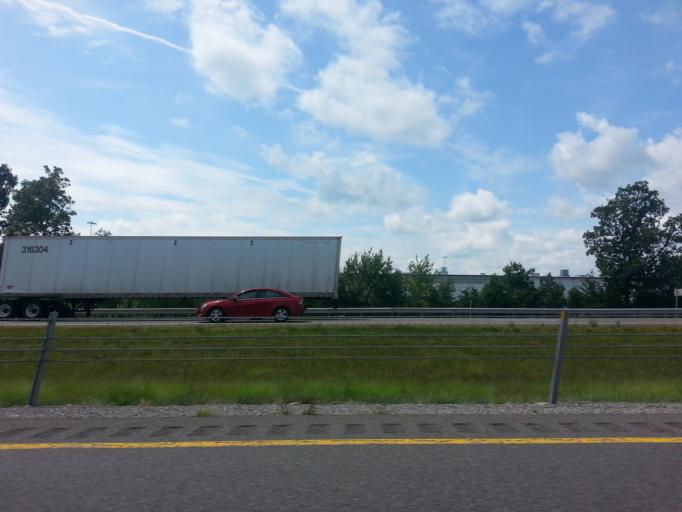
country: US
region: Tennessee
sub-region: Cumberland County
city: Crossville
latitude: 36.0025
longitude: -85.0485
